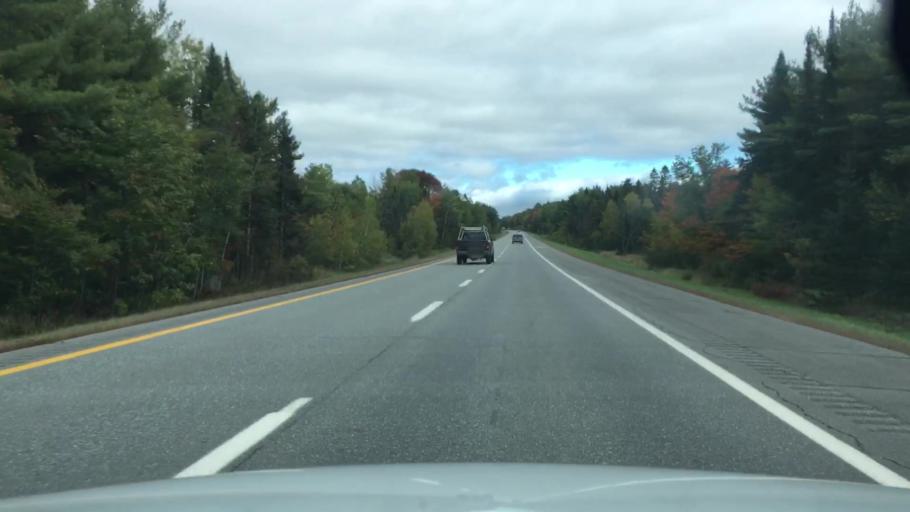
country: US
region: Maine
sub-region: Penobscot County
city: Carmel
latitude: 44.7753
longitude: -69.0423
